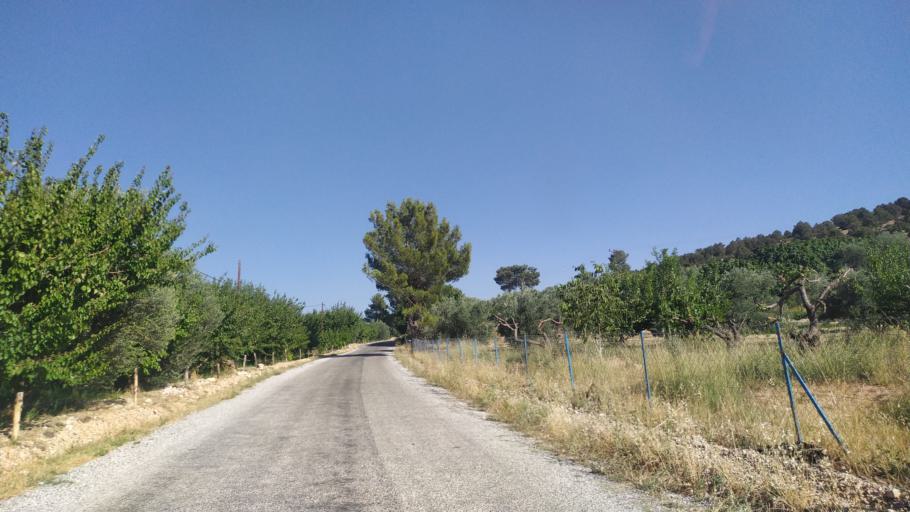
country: TR
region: Mersin
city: Mut
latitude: 36.7019
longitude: 33.4774
